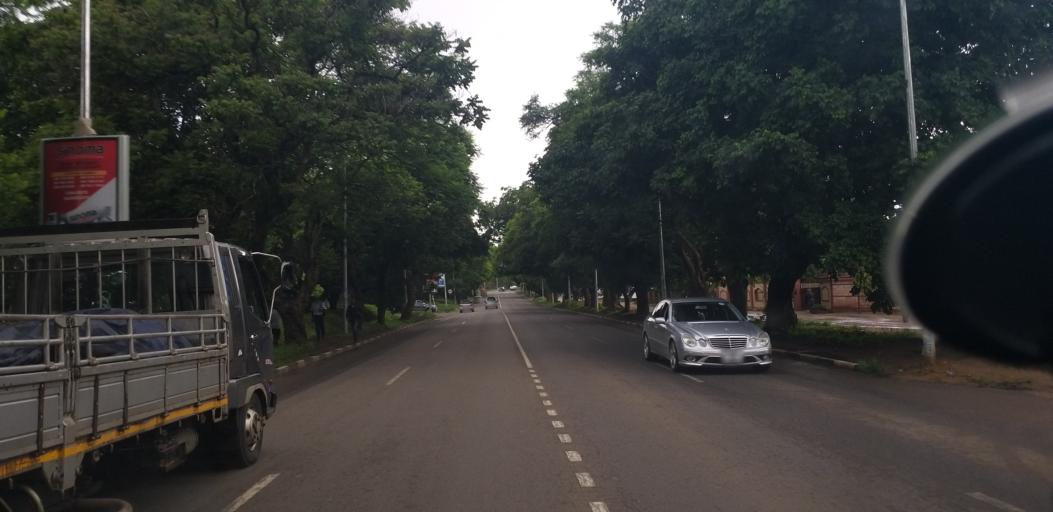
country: ZM
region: Lusaka
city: Lusaka
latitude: -15.4151
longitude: 28.2928
